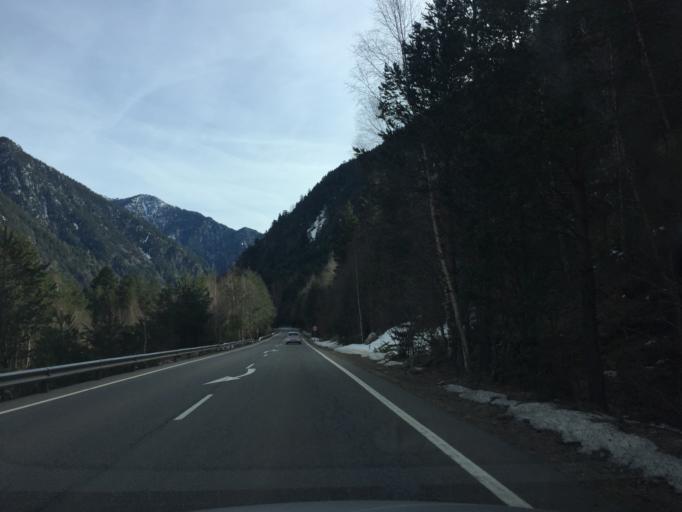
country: ES
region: Aragon
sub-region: Provincia de Huesca
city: Bielsa
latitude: 42.6945
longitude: 0.2031
